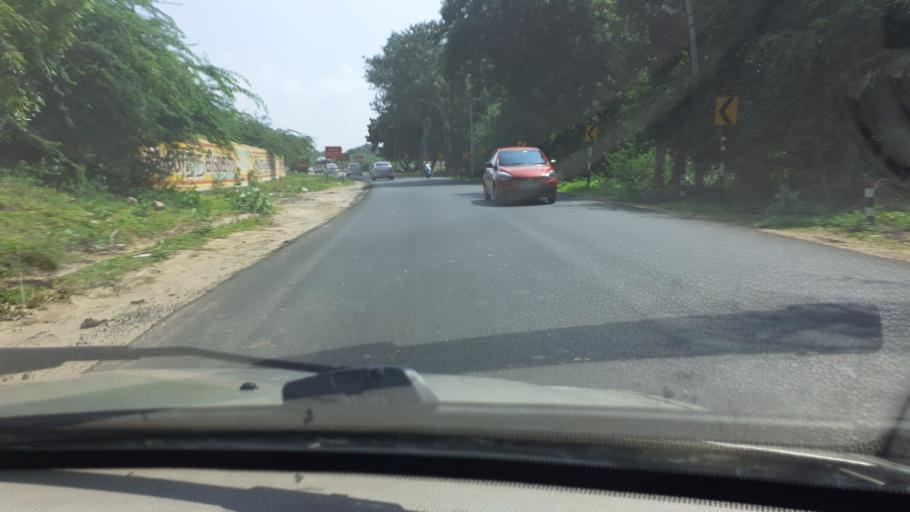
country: IN
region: Tamil Nadu
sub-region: Thoothukkudi
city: Alwar Tirunagari
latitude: 8.6085
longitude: 77.9304
